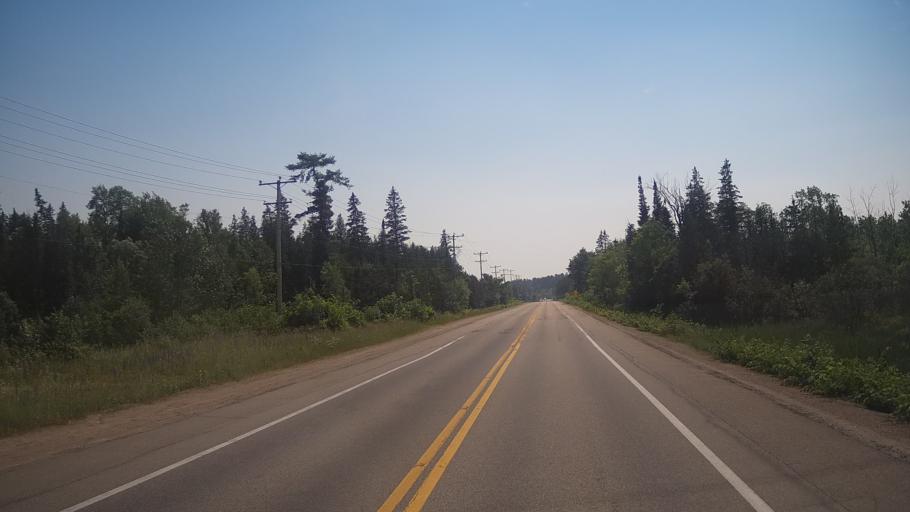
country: CA
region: Ontario
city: Pembroke
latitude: 45.8217
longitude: -77.0208
